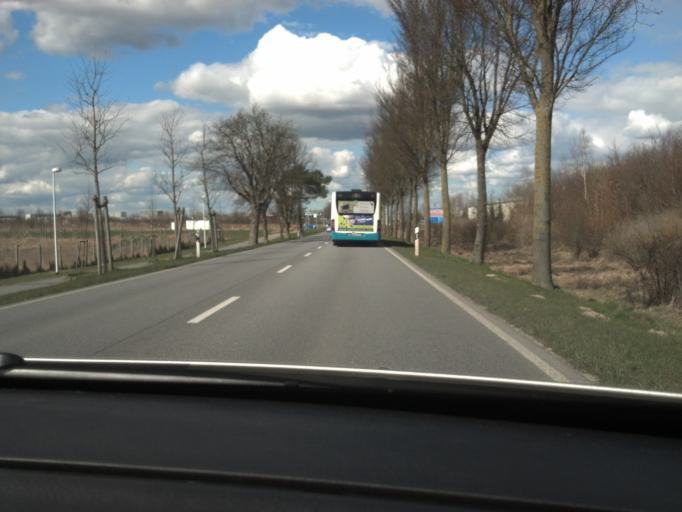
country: DE
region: Mecklenburg-Vorpommern
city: Burg Stargard
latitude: 53.5405
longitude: 13.3148
